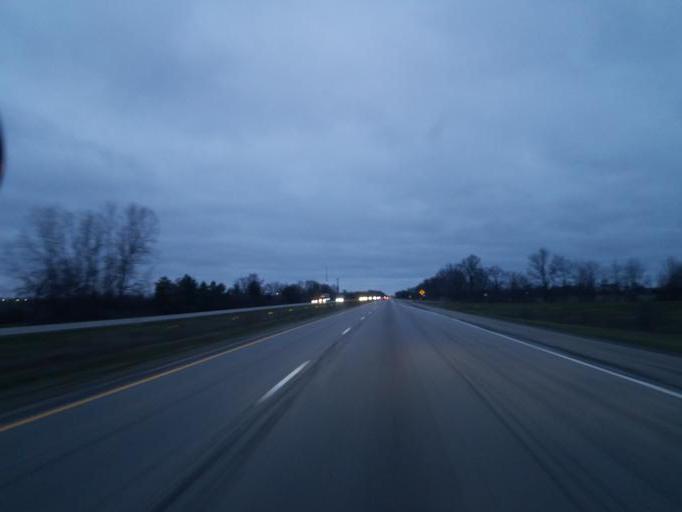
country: US
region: Michigan
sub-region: Washtenaw County
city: Milan
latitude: 42.1578
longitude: -83.6839
